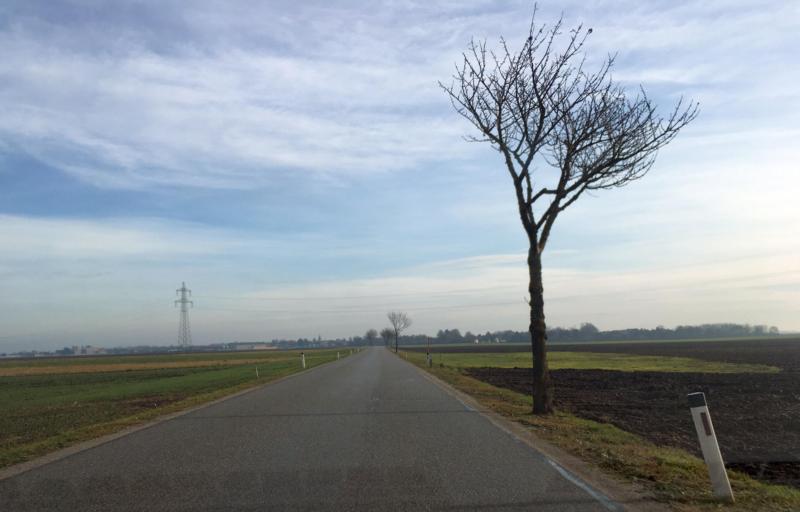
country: AT
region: Lower Austria
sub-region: Politischer Bezirk Ganserndorf
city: Leopoldsdorf im Marchfelde
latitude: 48.1945
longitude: 16.6938
